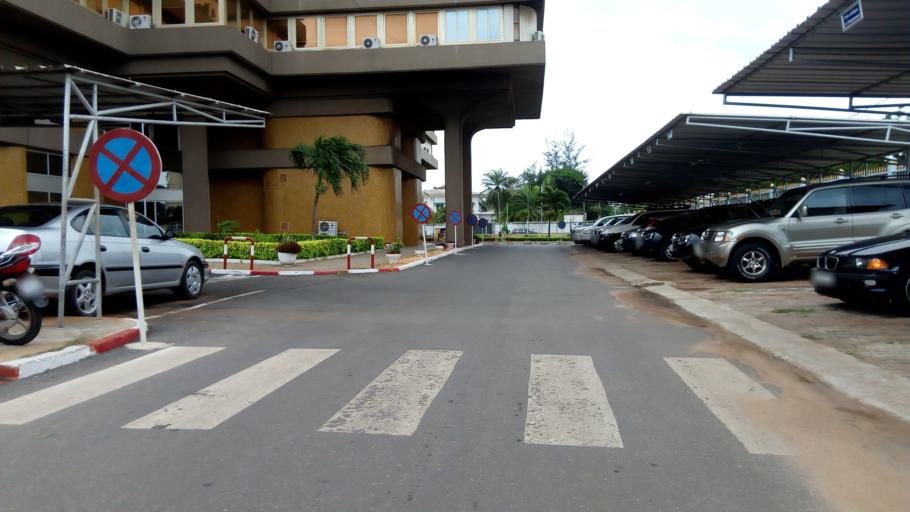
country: TG
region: Maritime
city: Lome
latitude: 6.1275
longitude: 1.2173
